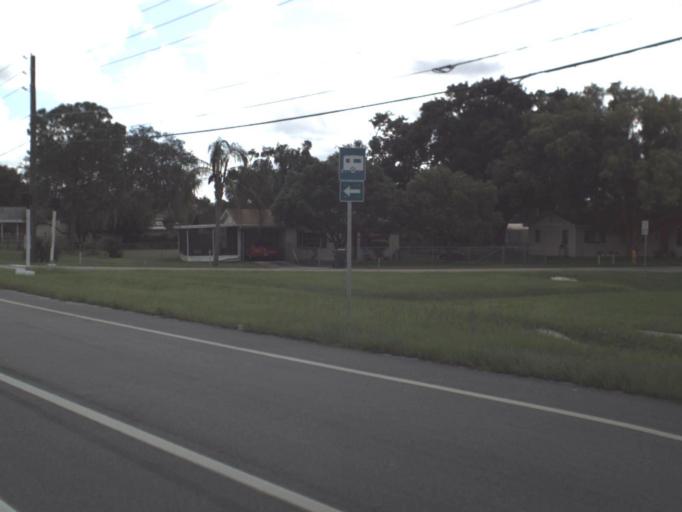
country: US
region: Florida
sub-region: Polk County
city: Gibsonia
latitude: 28.1066
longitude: -81.9384
